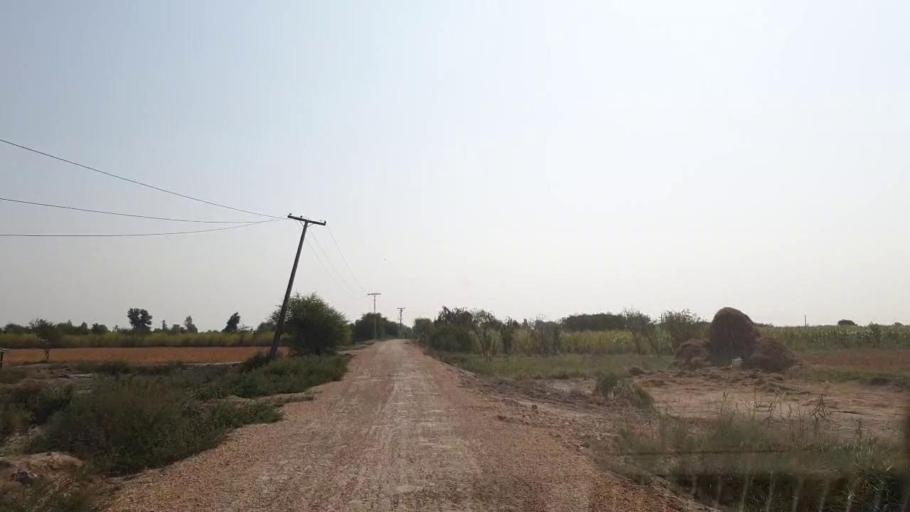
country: PK
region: Sindh
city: Tando Muhammad Khan
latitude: 25.0418
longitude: 68.4544
